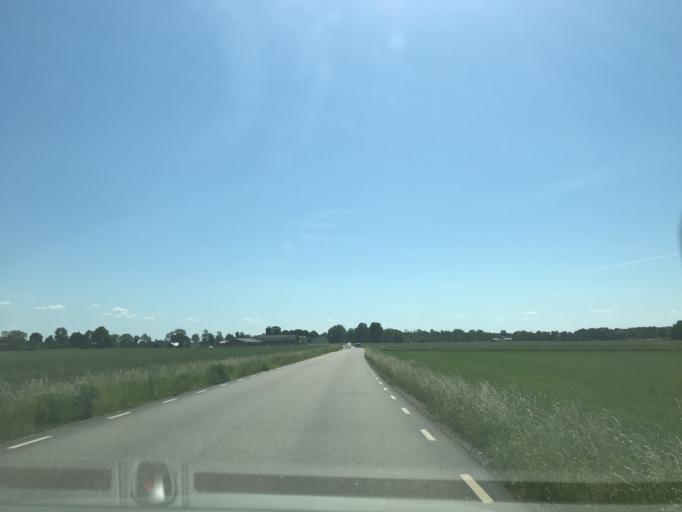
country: SE
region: Vaestra Goetaland
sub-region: Gotene Kommun
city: Kallby
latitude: 58.5200
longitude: 13.3214
